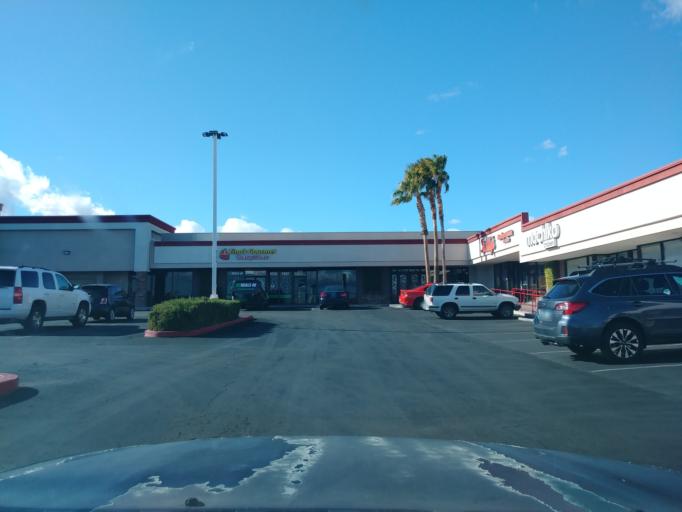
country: US
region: Nevada
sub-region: Clark County
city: Spring Valley
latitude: 36.1487
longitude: -115.2093
